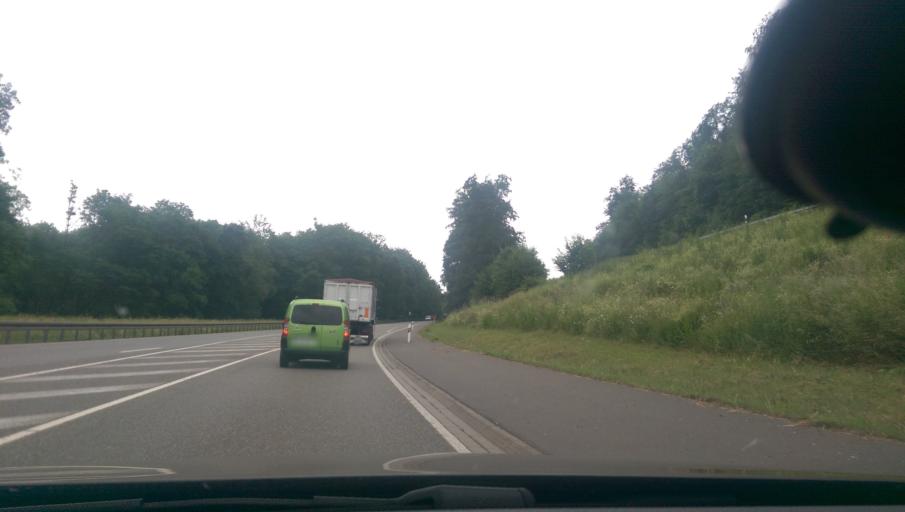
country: DE
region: Thuringia
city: Sondershausen
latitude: 51.3414
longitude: 10.8266
